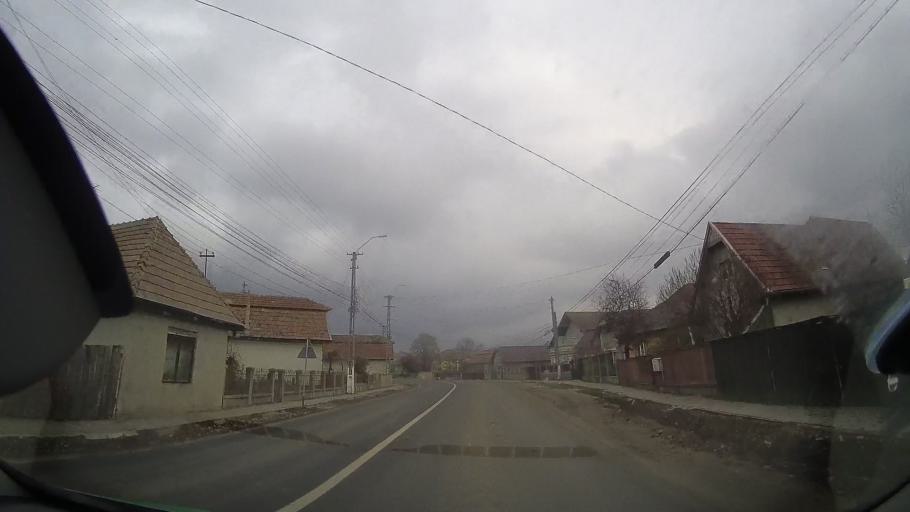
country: RO
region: Cluj
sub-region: Comuna Mihai Viteazu
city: Mihai Viteazu
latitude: 46.5408
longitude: 23.7557
